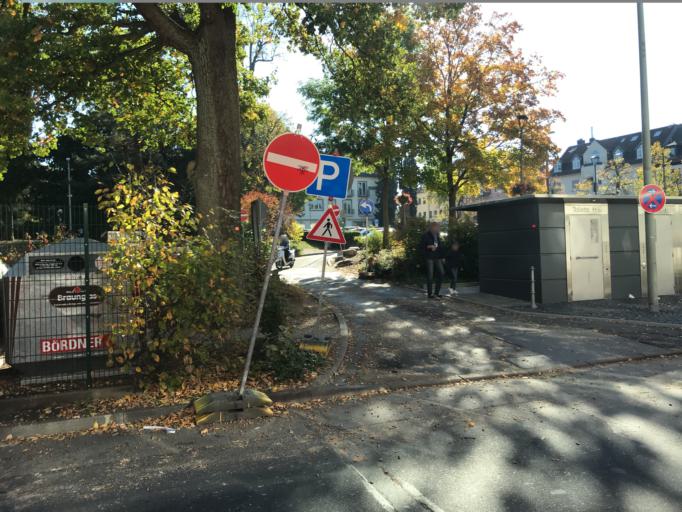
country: DE
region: Hesse
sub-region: Regierungsbezirk Darmstadt
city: Konigstein im Taunus
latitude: 50.1829
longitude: 8.4671
